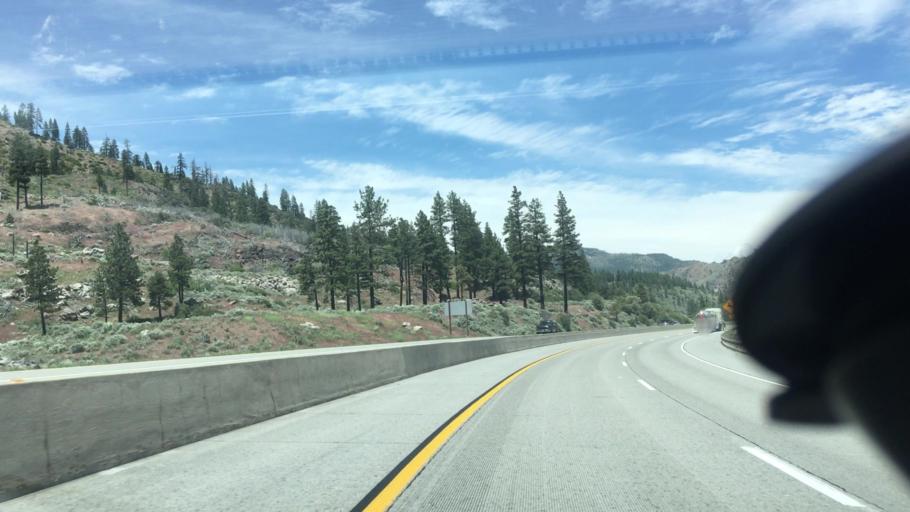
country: US
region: Nevada
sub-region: Washoe County
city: Verdi
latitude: 39.3860
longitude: -120.0249
